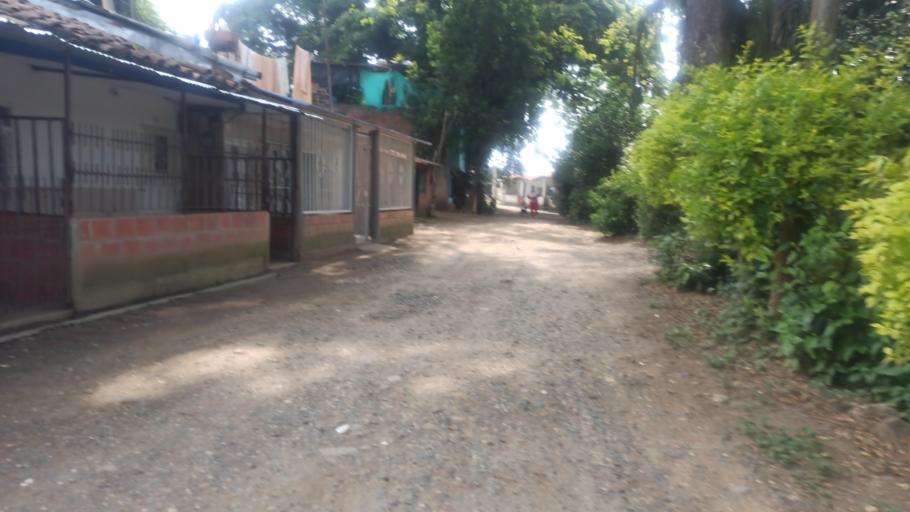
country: CO
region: Valle del Cauca
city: Jamundi
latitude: 3.2004
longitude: -76.5013
